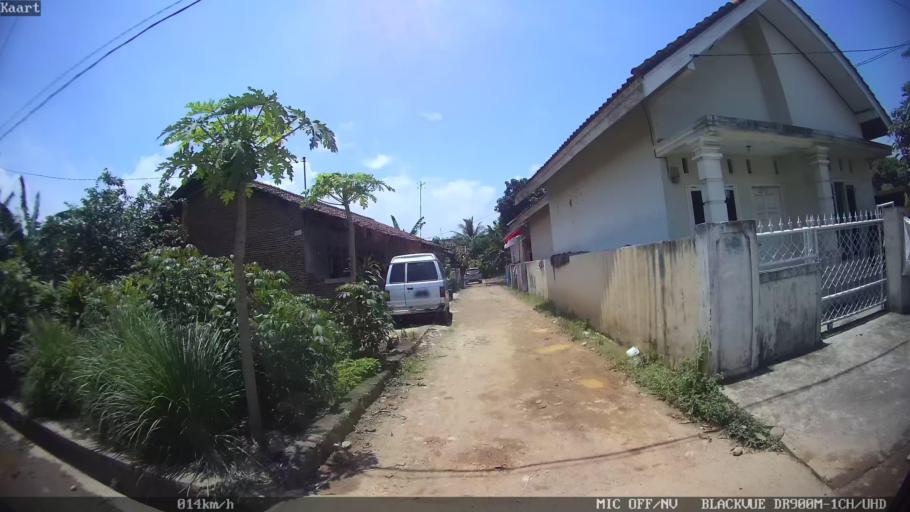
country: ID
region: Lampung
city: Kedaton
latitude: -5.3735
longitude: 105.2838
